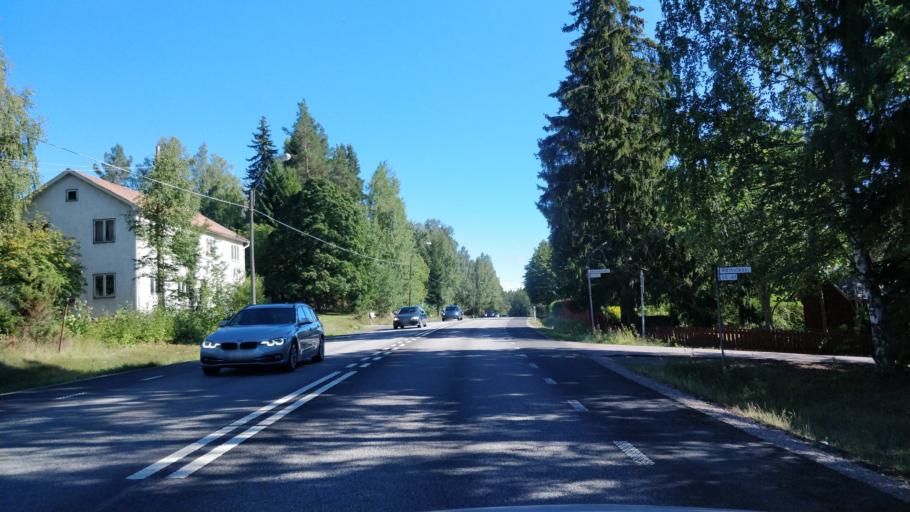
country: SE
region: Dalarna
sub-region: Faluns Kommun
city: Grycksbo
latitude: 60.6946
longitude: 15.4843
